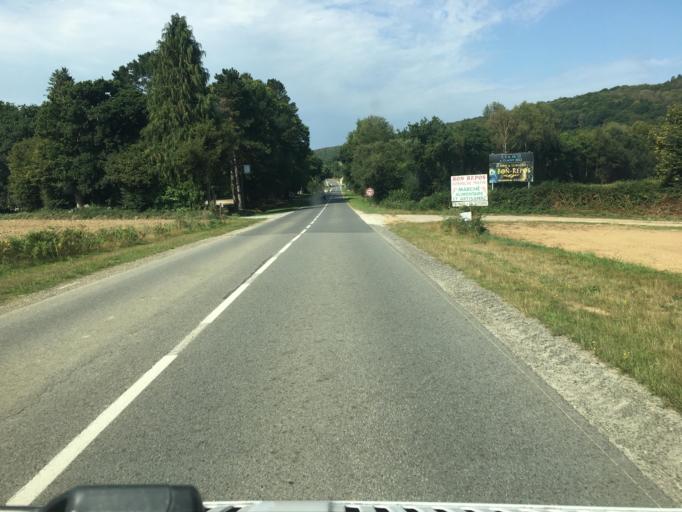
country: FR
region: Brittany
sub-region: Departement des Cotes-d'Armor
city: Gouarec
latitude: 48.2141
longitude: -3.1206
